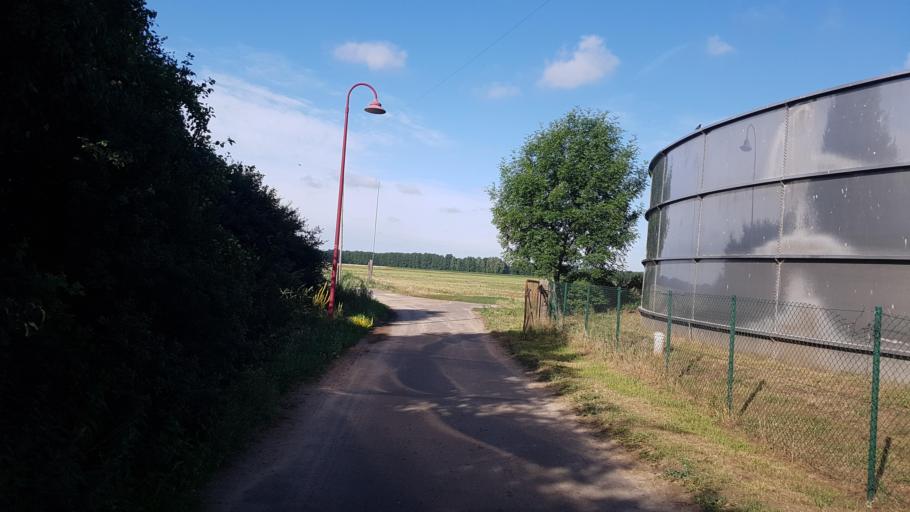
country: DE
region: Brandenburg
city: Trebbin
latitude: 52.1863
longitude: 13.1613
